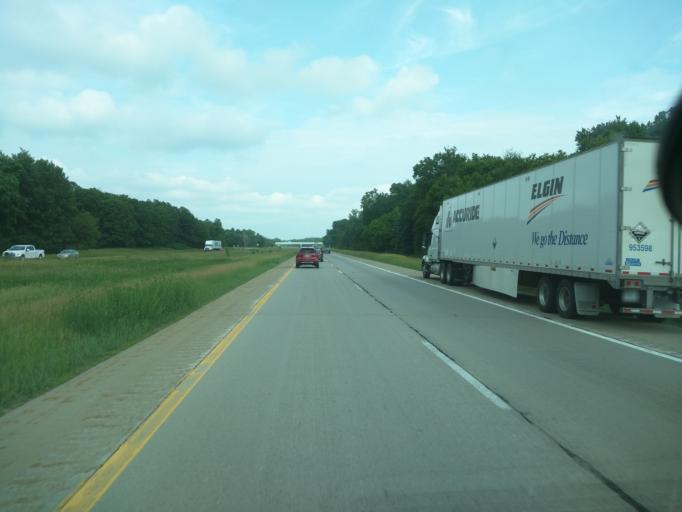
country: US
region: Michigan
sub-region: Clinton County
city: Bath
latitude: 42.8005
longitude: -84.4589
